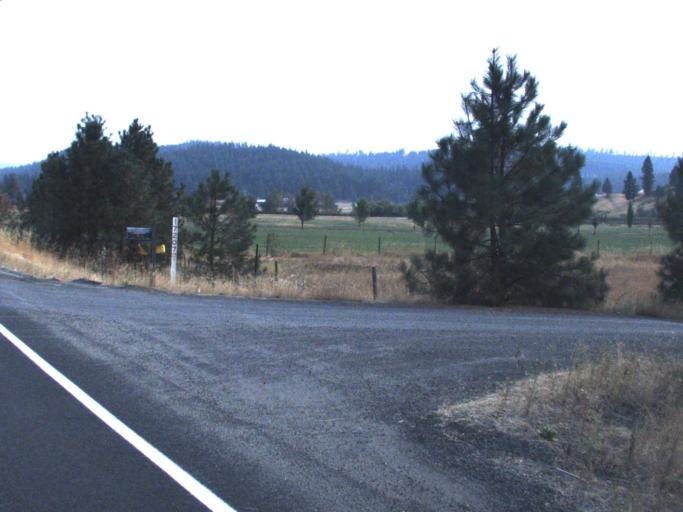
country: US
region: Washington
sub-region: Spokane County
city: Trentwood
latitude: 47.8145
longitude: -117.2145
